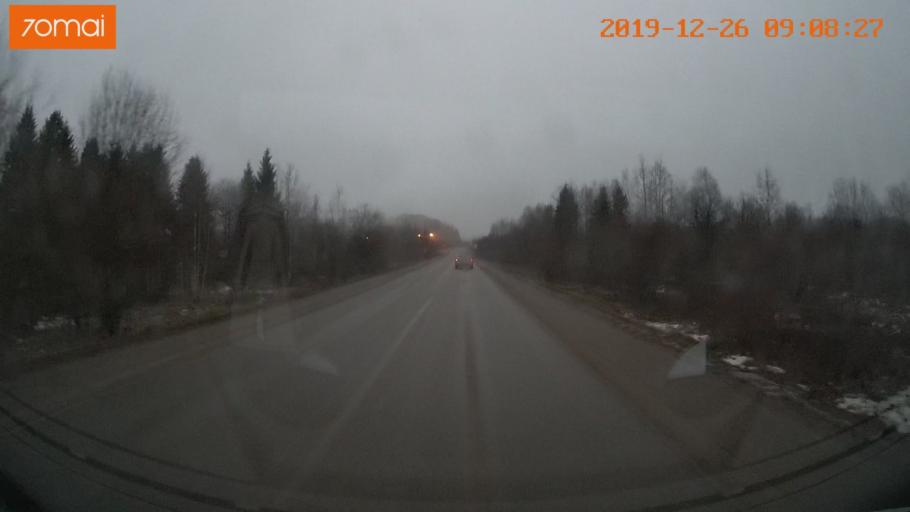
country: RU
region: Vologda
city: Gryazovets
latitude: 58.8568
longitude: 40.2484
